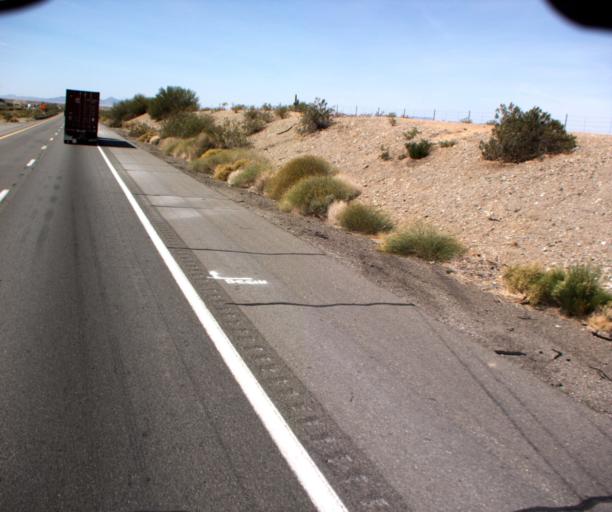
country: US
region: Arizona
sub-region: La Paz County
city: Ehrenberg
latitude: 33.6172
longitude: -114.4595
